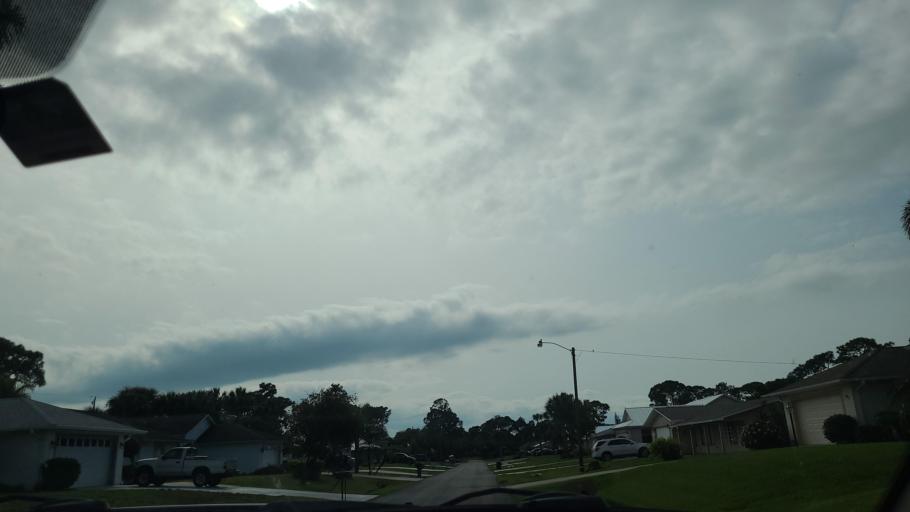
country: US
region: Florida
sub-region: Indian River County
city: Sebastian
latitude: 27.7866
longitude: -80.4819
